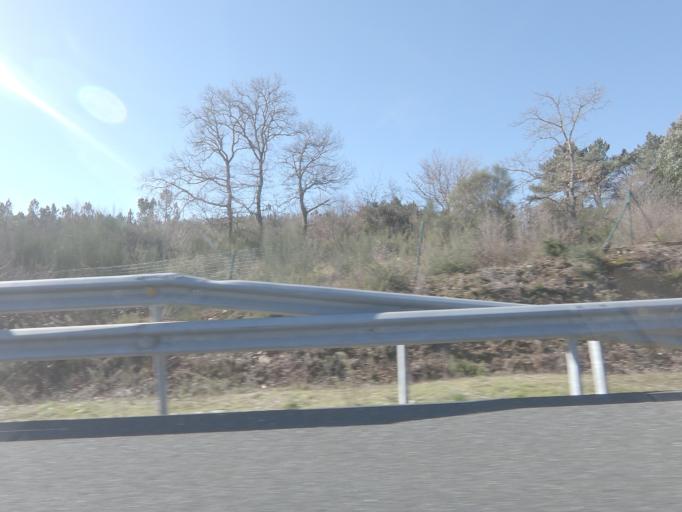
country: ES
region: Galicia
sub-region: Provincia de Ourense
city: Pinor
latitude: 42.5392
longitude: -8.0175
